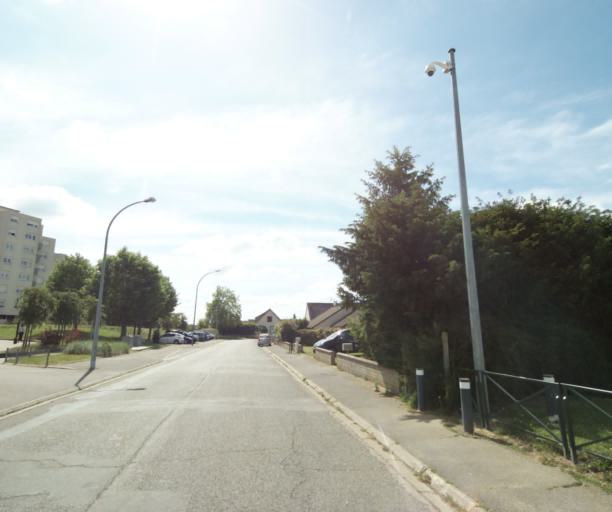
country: FR
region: Centre
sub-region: Departement d'Eure-et-Loir
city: Mainvilliers
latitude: 48.4382
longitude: 1.4457
